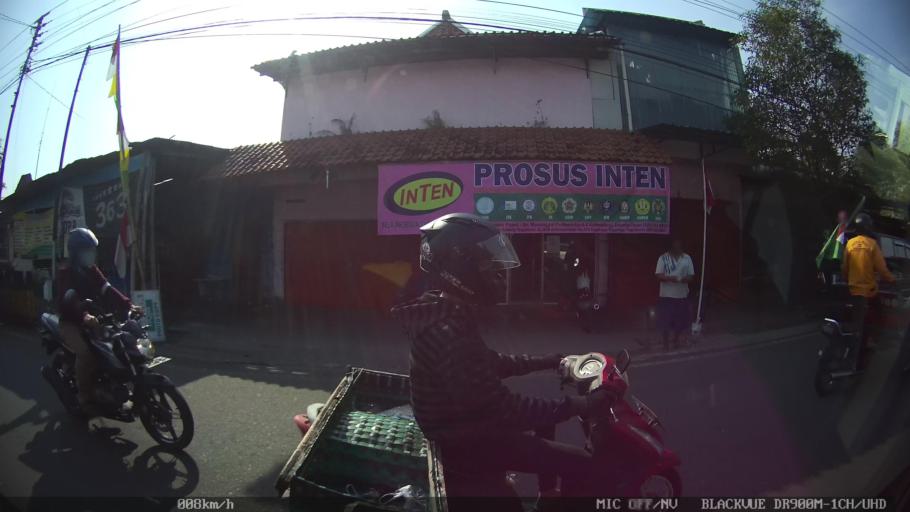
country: ID
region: Daerah Istimewa Yogyakarta
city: Yogyakarta
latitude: -7.7887
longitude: 110.3541
